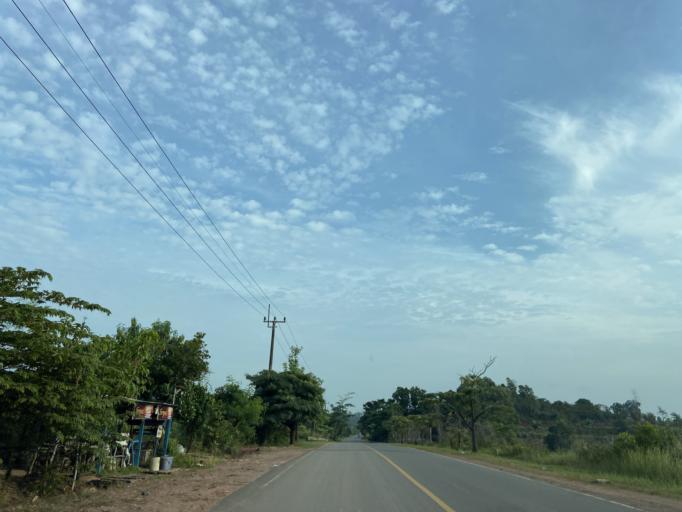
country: ID
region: Riau Islands
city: Tanjungpinang
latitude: 0.9154
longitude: 104.1203
